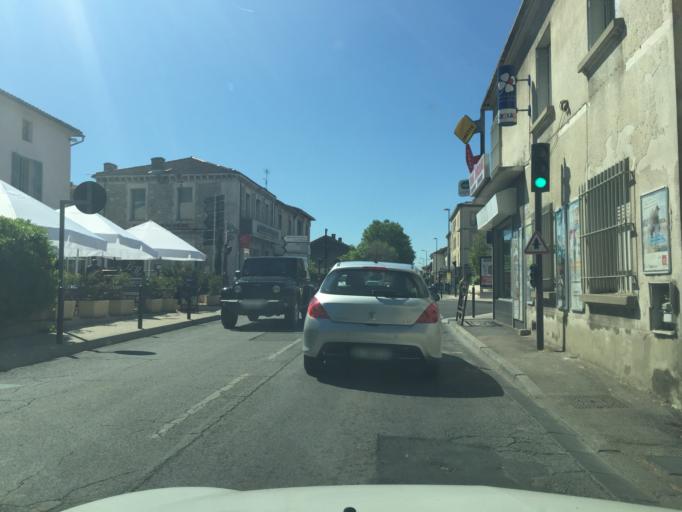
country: FR
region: Provence-Alpes-Cote d'Azur
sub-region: Departement du Vaucluse
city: Montfavet
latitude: 43.9362
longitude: 4.8717
